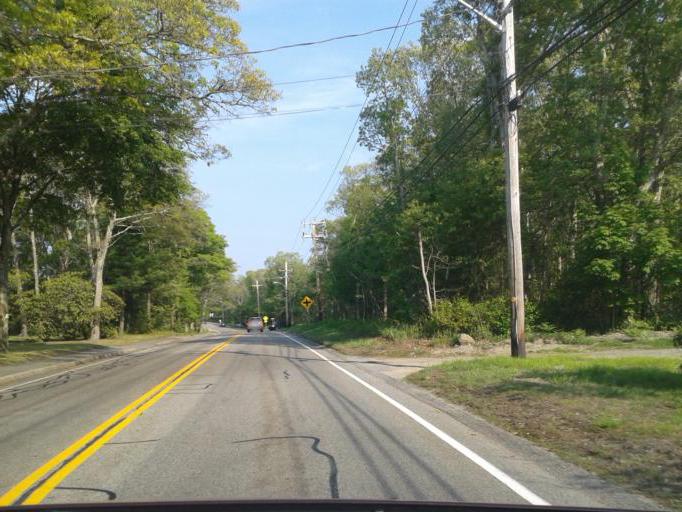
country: US
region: Massachusetts
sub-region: Barnstable County
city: Teaticket
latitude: 41.5840
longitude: -70.6015
